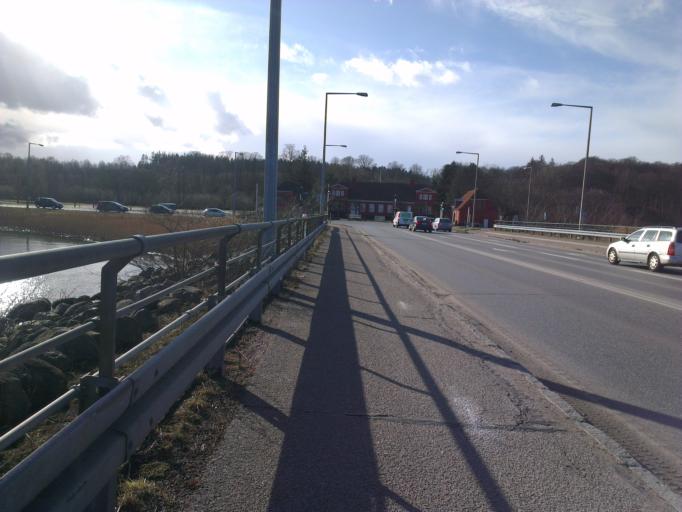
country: DK
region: Capital Region
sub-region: Frederikssund Kommune
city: Frederikssund
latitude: 55.8417
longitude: 12.0341
